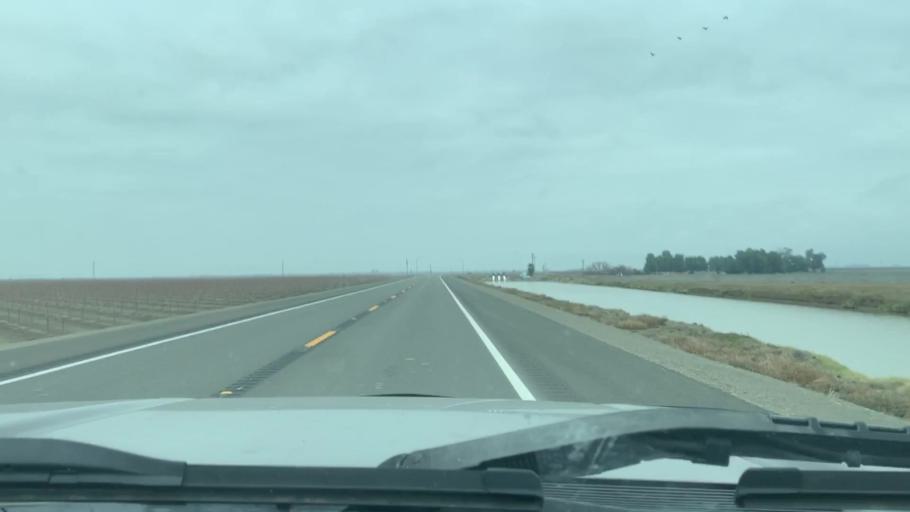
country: US
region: California
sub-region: Kings County
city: Stratford
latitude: 36.1343
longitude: -119.8820
